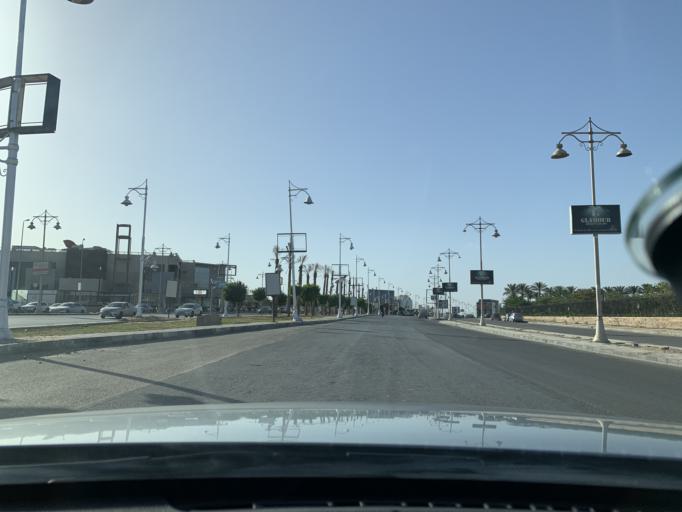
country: EG
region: Muhafazat al Qalyubiyah
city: Al Khankah
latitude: 30.0196
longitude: 31.4966
